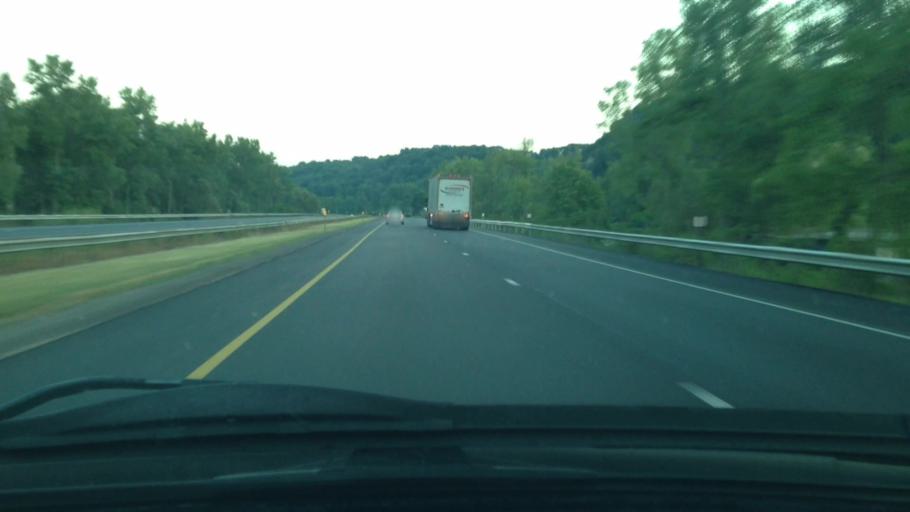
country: US
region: New York
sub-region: Montgomery County
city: Fort Plain
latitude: 42.9240
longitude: -74.6138
